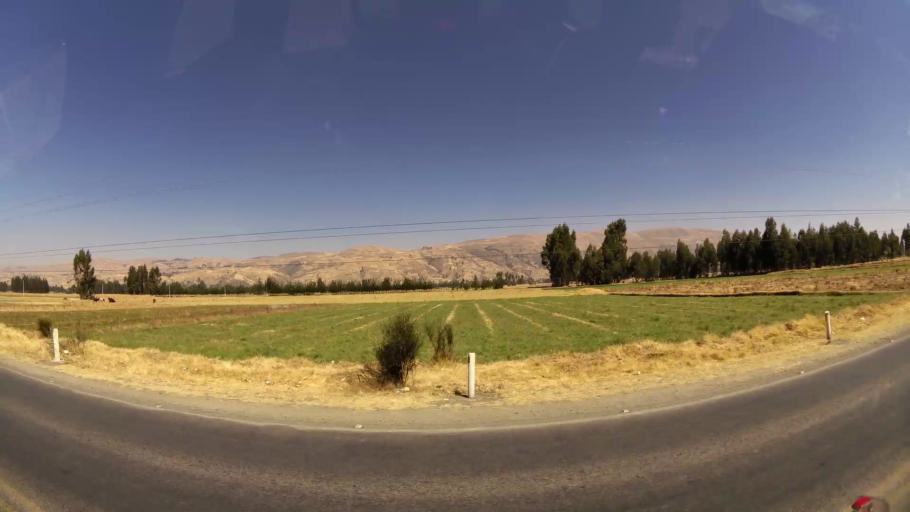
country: PE
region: Junin
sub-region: Provincia de Jauja
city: San Lorenzo
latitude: -11.8596
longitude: -75.3766
